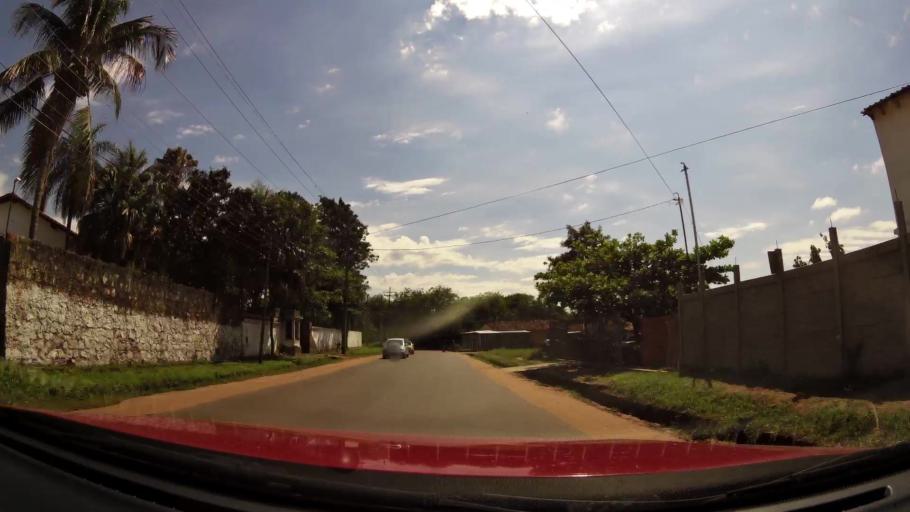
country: PY
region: Central
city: Limpio
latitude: -25.2514
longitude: -57.4917
